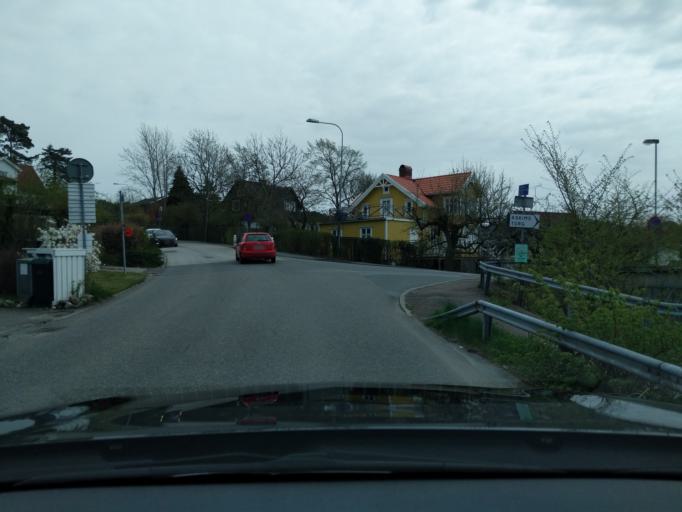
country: SE
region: Vaestra Goetaland
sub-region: Goteborg
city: Majorna
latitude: 57.6348
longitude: 11.9378
